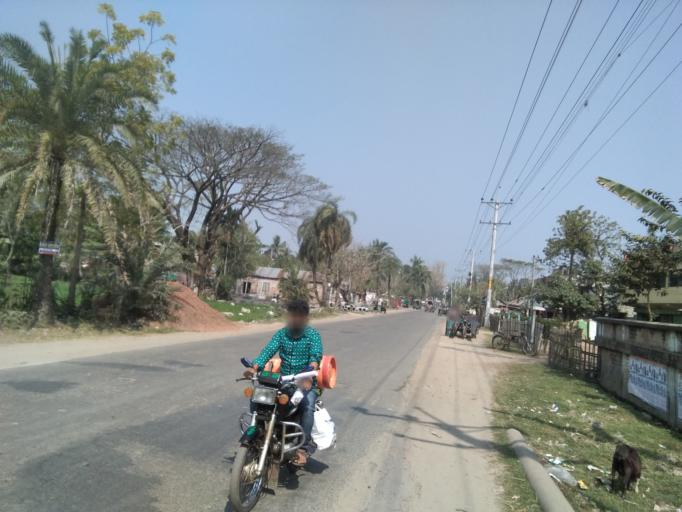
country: IN
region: West Bengal
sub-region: North 24 Parganas
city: Taki
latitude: 22.5919
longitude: 89.0006
